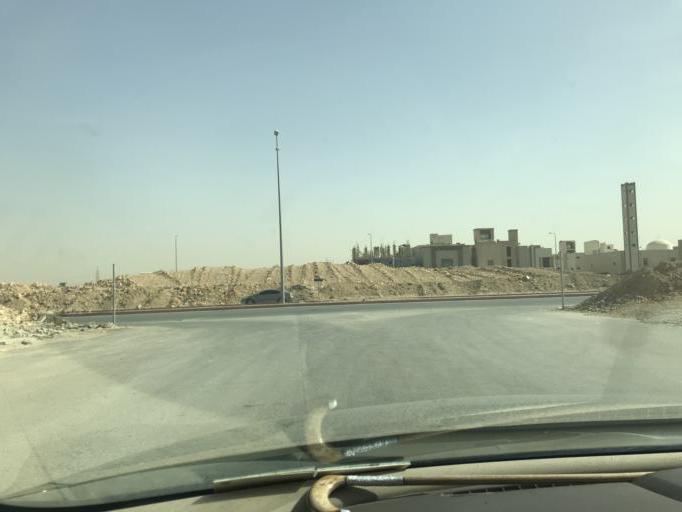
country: SA
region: Ar Riyad
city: Riyadh
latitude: 24.8255
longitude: 46.7304
